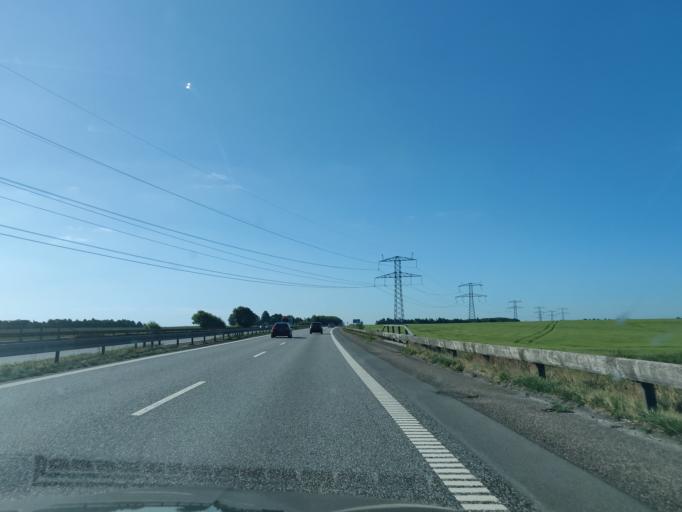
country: DK
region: Central Jutland
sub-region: Randers Kommune
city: Spentrup
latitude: 56.5047
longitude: 9.9747
